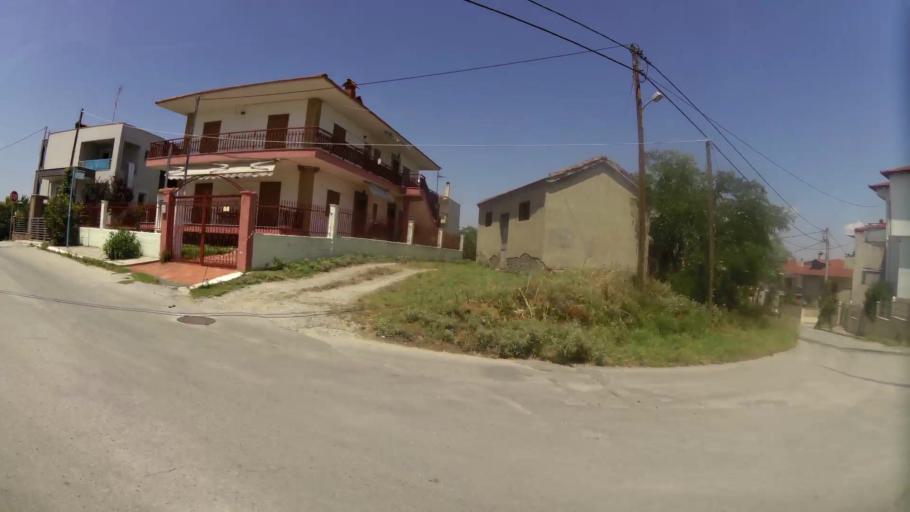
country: GR
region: Central Macedonia
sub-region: Nomos Thessalonikis
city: Trilofos
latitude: 40.4642
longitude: 22.9676
